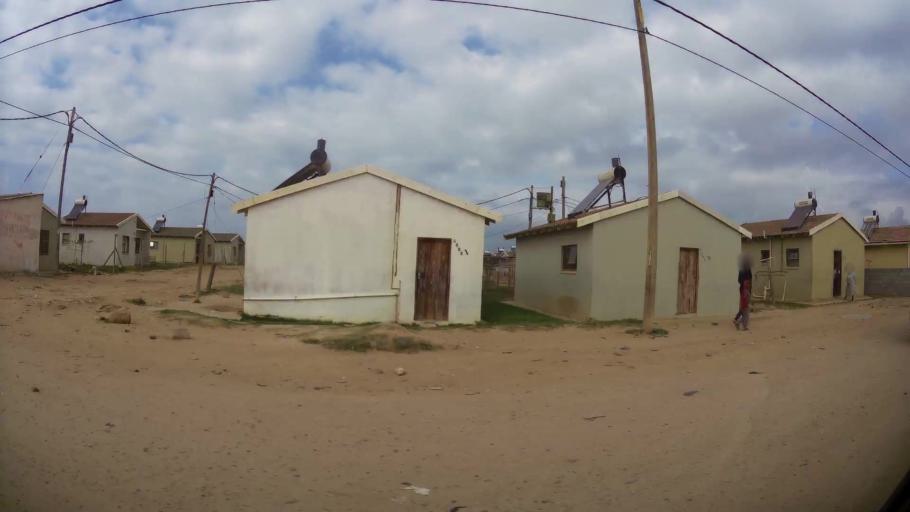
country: ZA
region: Eastern Cape
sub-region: Nelson Mandela Bay Metropolitan Municipality
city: Port Elizabeth
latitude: -33.8297
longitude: 25.6298
